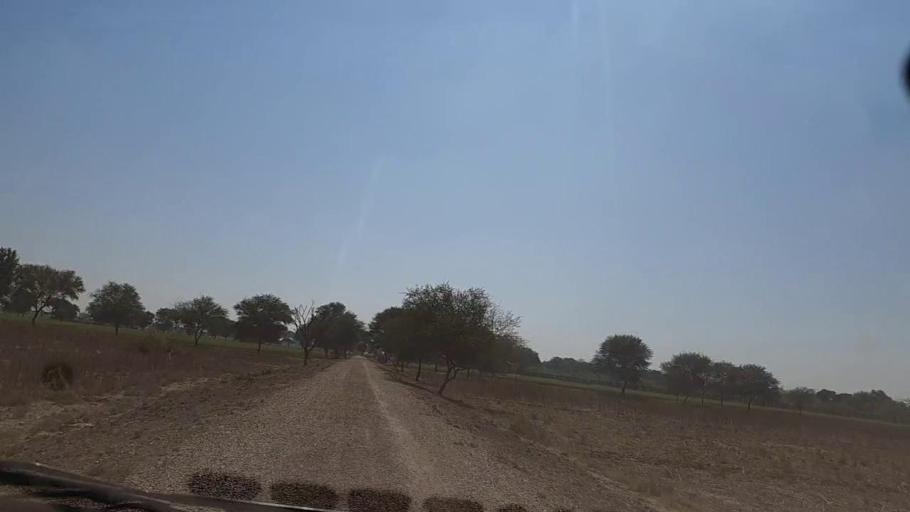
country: PK
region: Sindh
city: Mirpur Khas
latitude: 25.4368
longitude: 69.0480
